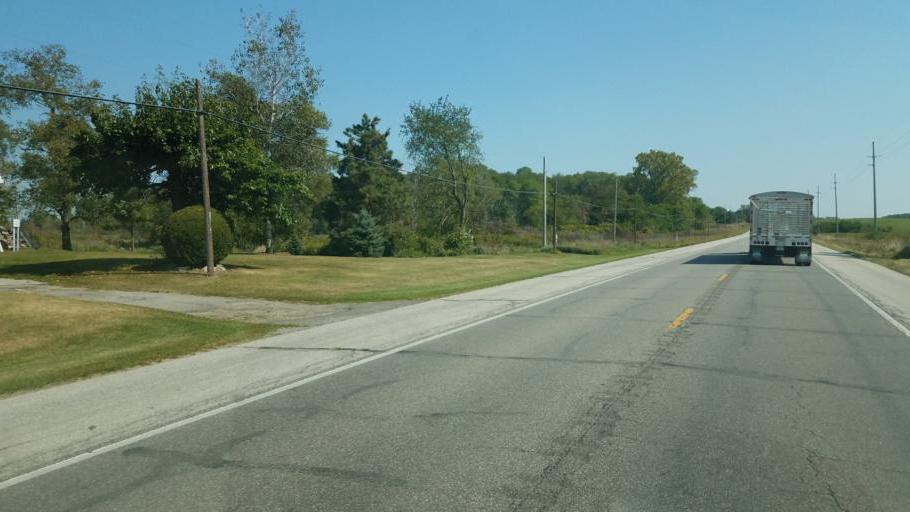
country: US
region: Indiana
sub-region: LaGrange County
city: Lagrange
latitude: 41.6421
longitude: -85.3199
